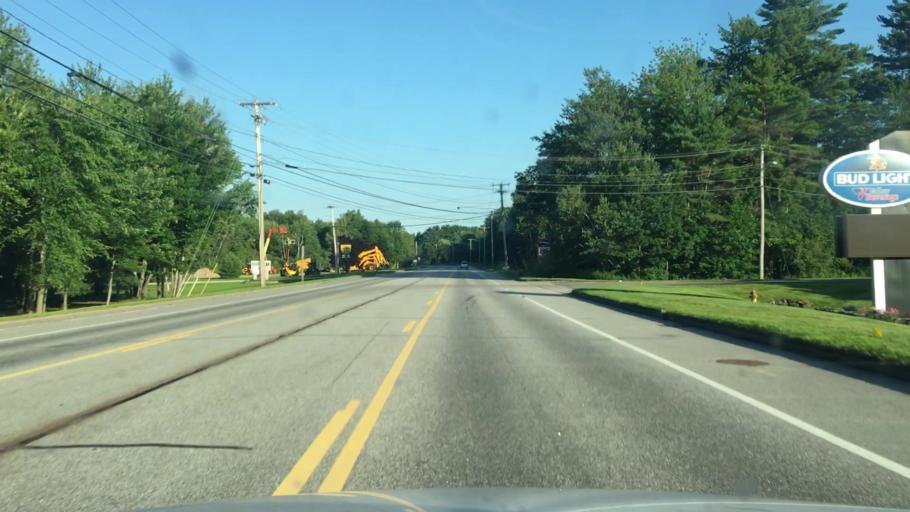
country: US
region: Maine
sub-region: Androscoggin County
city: Lisbon
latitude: 44.0550
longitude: -70.1398
